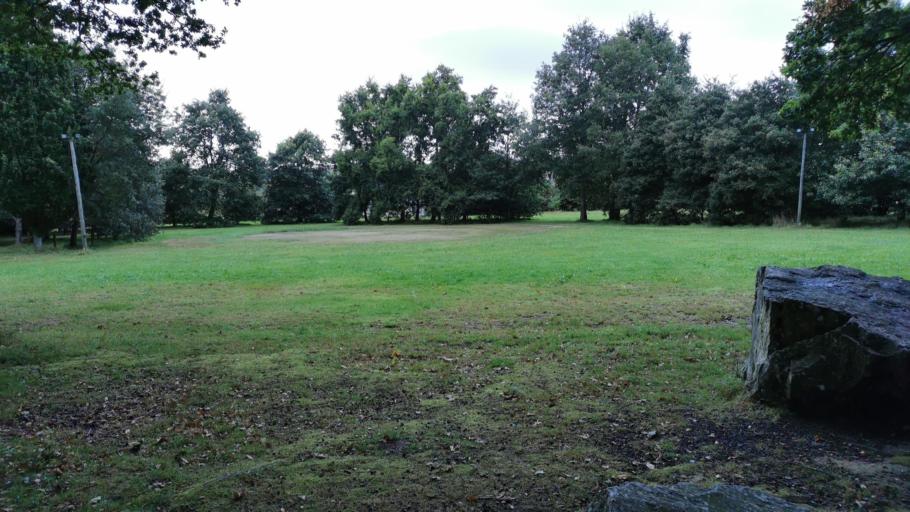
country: FR
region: Brittany
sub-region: Departement des Cotes-d'Armor
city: Pleslin-Trigavou
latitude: 48.5293
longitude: -2.0580
